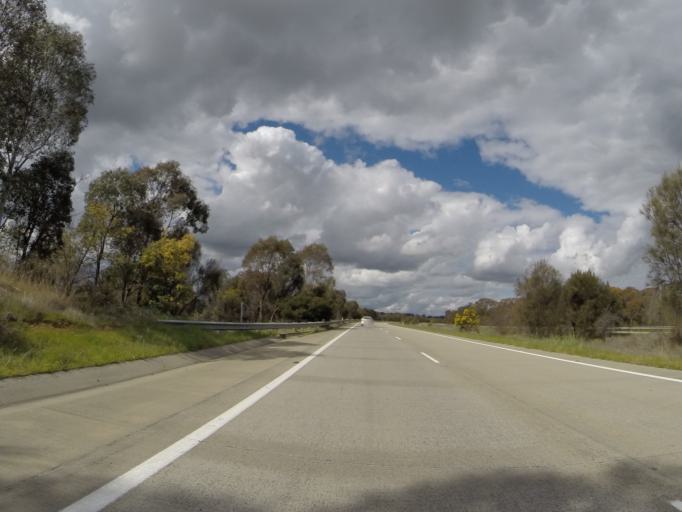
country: AU
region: New South Wales
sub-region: Yass Valley
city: Gundaroo
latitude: -34.7881
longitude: 149.2002
